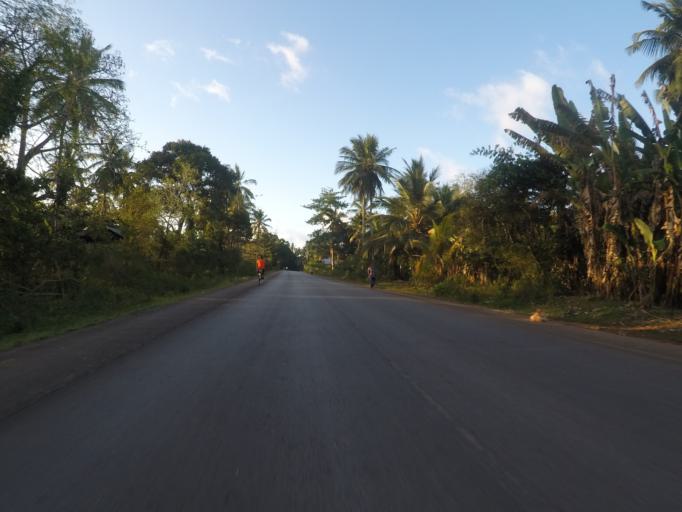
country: TZ
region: Zanzibar Central/South
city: Koani
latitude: -6.1773
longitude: 39.3292
